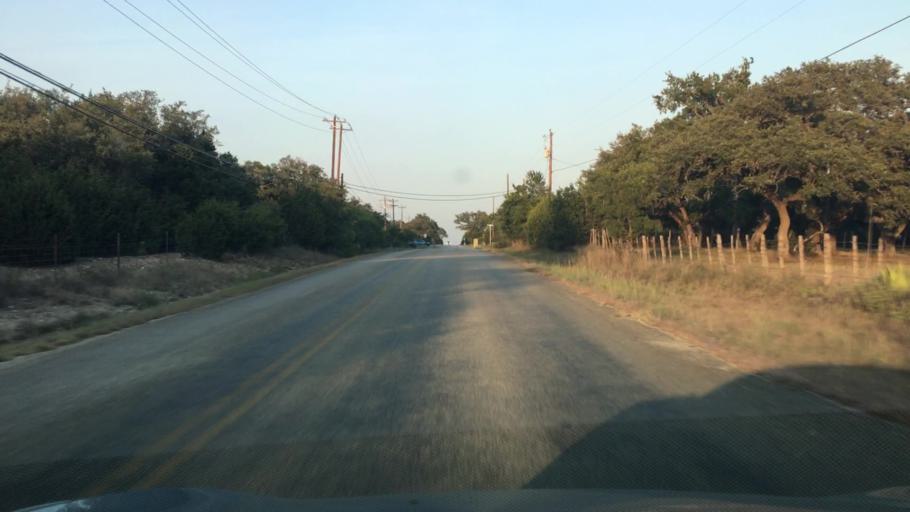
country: US
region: Texas
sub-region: Hays County
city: Dripping Springs
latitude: 30.1534
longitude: -98.0114
